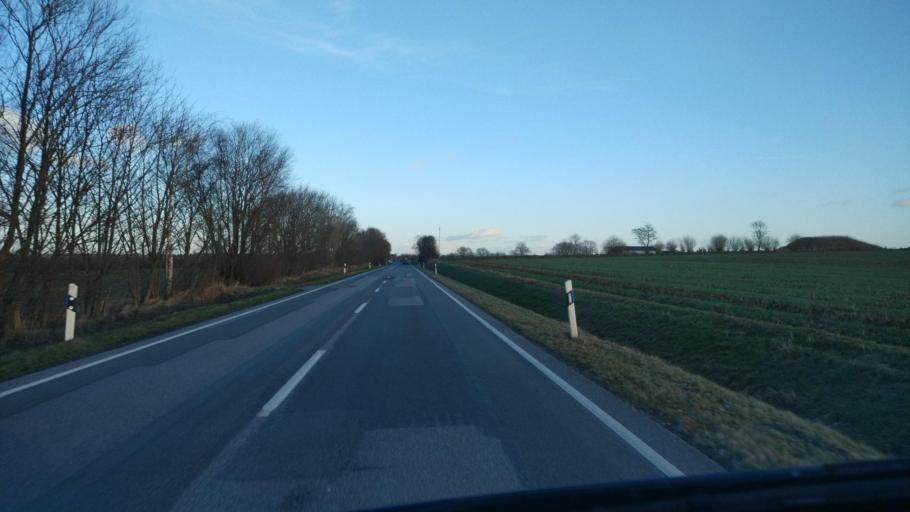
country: DE
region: Schleswig-Holstein
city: Wittbek
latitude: 54.4618
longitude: 9.1928
